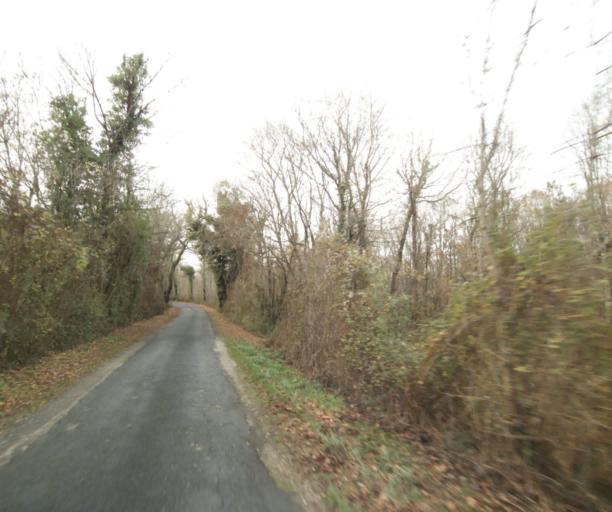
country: FR
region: Poitou-Charentes
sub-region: Departement de la Charente-Maritime
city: Fontcouverte
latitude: 45.7885
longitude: -0.5894
